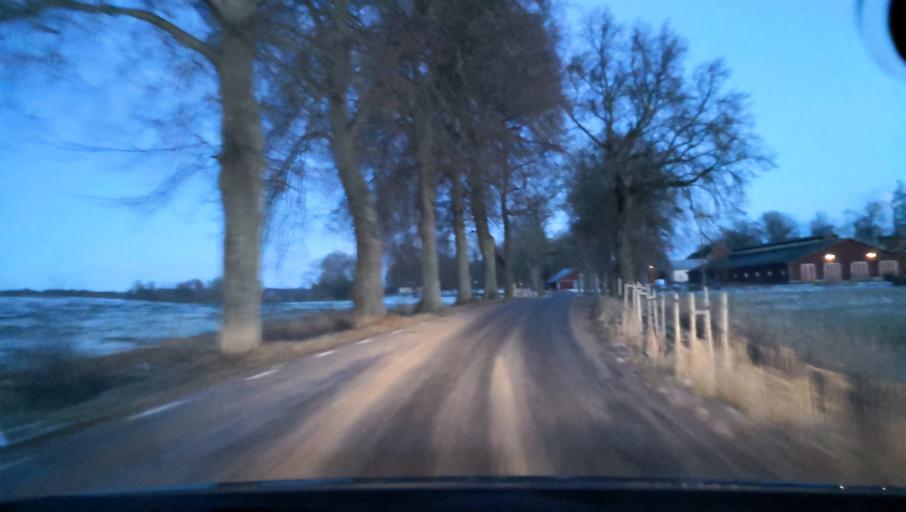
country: SE
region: Soedermanland
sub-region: Katrineholms Kommun
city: Katrineholm
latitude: 59.0854
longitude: 16.3090
